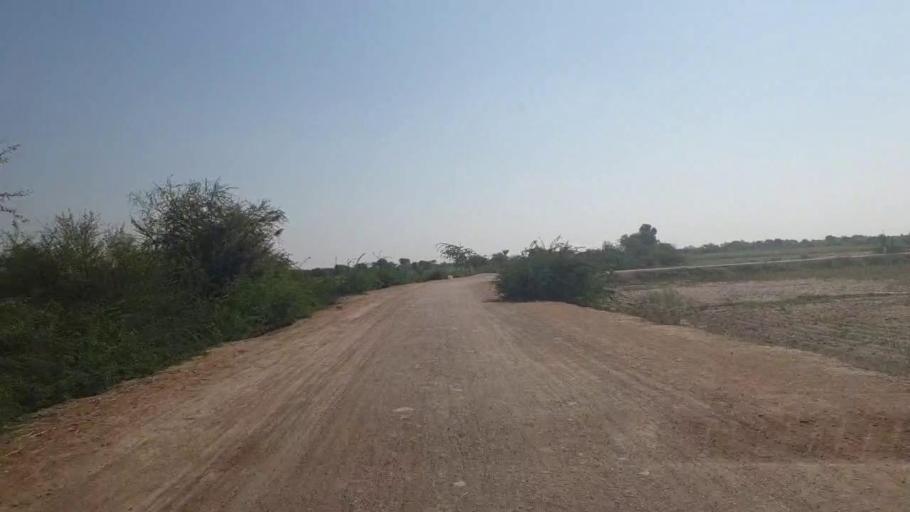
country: PK
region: Sindh
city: Badin
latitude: 24.5898
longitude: 68.8456
